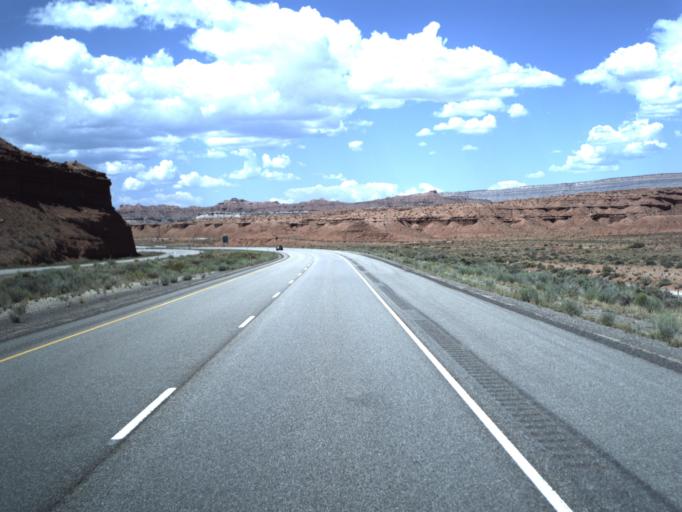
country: US
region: Utah
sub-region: Emery County
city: Ferron
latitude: 38.8455
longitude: -111.0533
